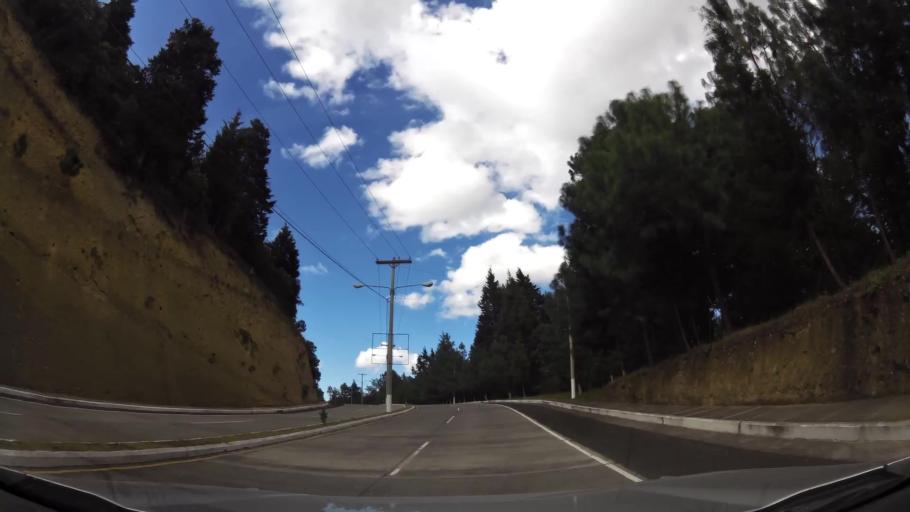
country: GT
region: Quetzaltenango
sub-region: Municipio de La Esperanza
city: La Esperanza
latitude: 14.8354
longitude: -91.5538
